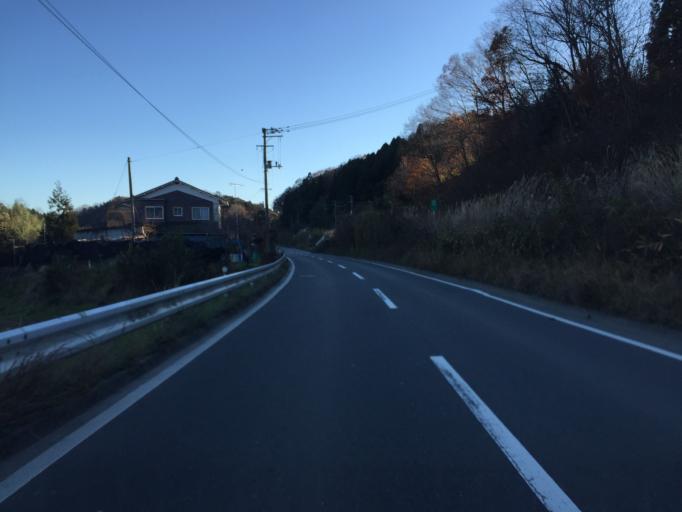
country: JP
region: Fukushima
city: Iwaki
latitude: 37.0950
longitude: 140.8600
